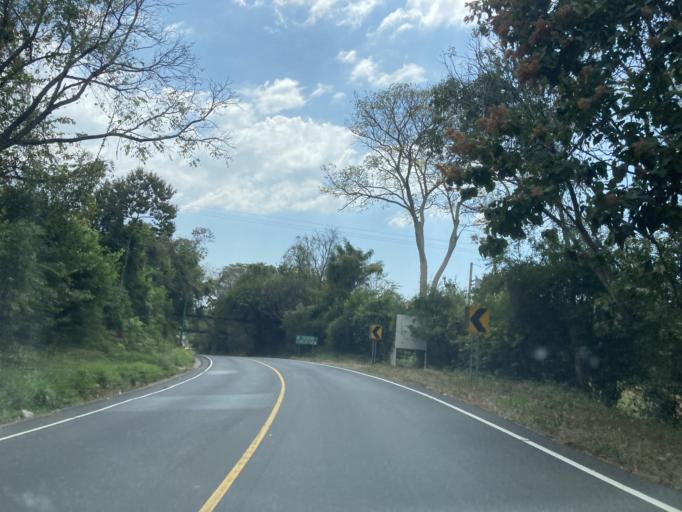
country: GT
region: Santa Rosa
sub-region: Municipio de Taxisco
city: Taxisco
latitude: 14.0661
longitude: -90.4709
